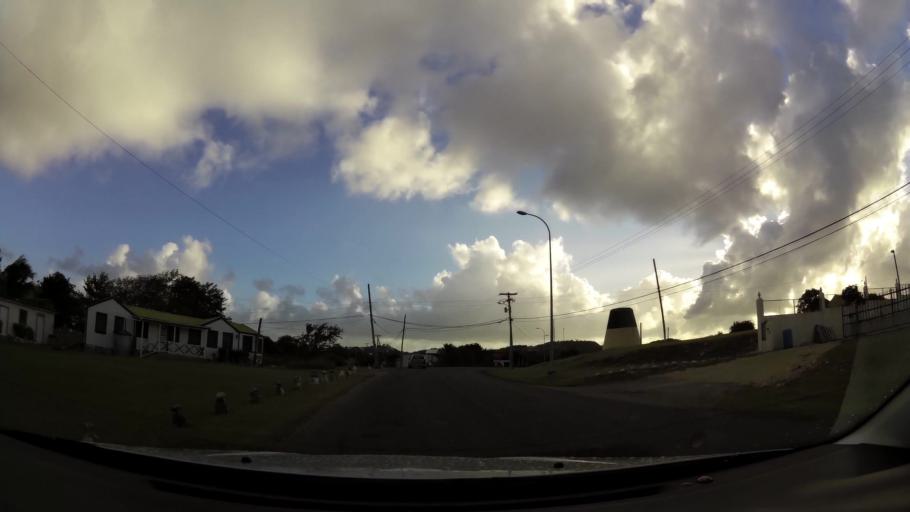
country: AG
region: Saint John
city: Saint John's
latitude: 17.1588
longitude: -61.8261
